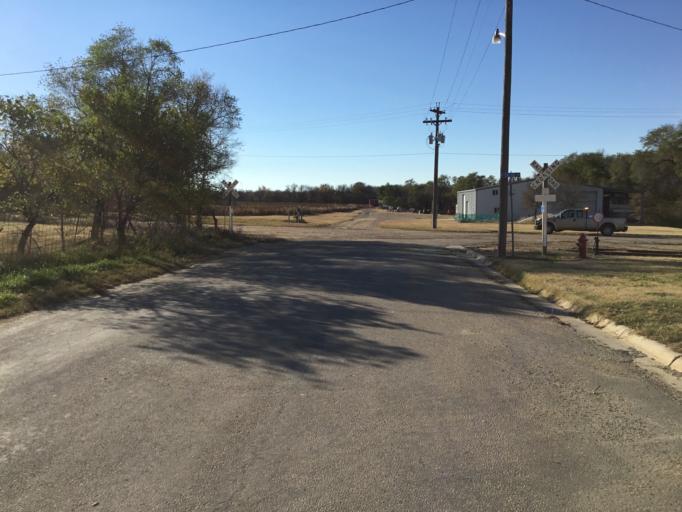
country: US
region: Kansas
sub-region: Lincoln County
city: Lincoln
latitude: 39.0342
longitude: -98.1427
